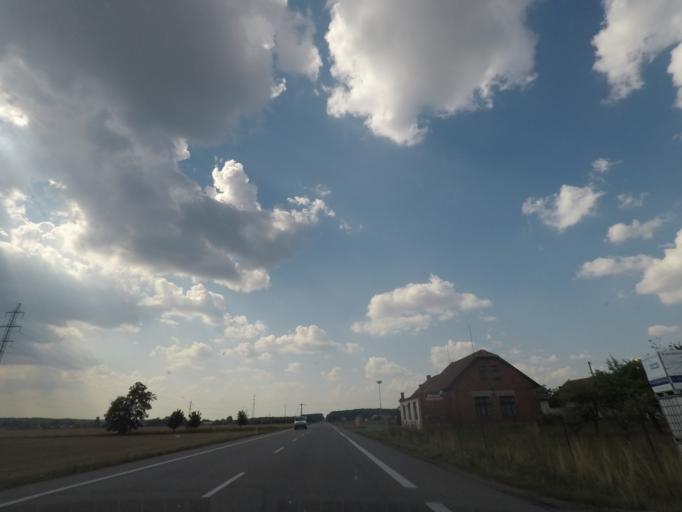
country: CZ
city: Albrechtice nad Orlici
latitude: 50.1670
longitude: 16.0467
